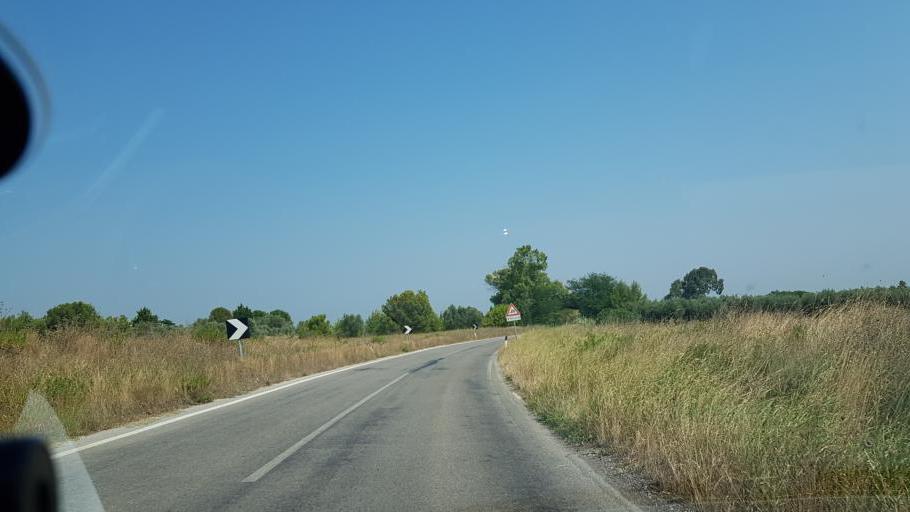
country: IT
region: Apulia
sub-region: Provincia di Brindisi
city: Torre Santa Susanna
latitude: 40.4975
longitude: 17.7505
